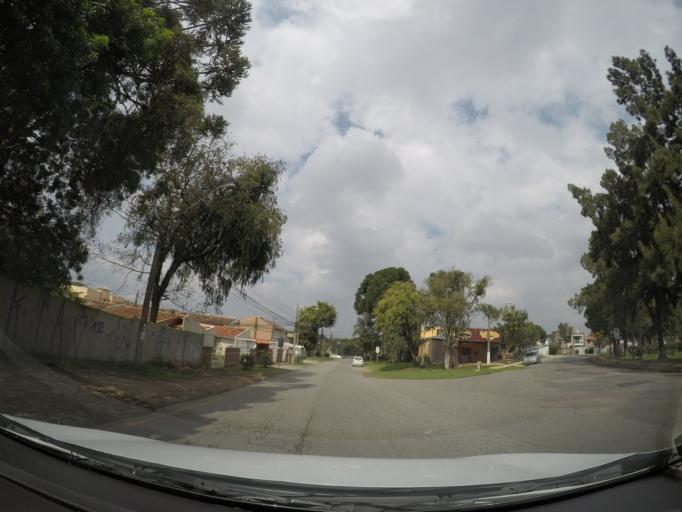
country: BR
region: Parana
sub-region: Sao Jose Dos Pinhais
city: Sao Jose dos Pinhais
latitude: -25.5053
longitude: -49.2468
